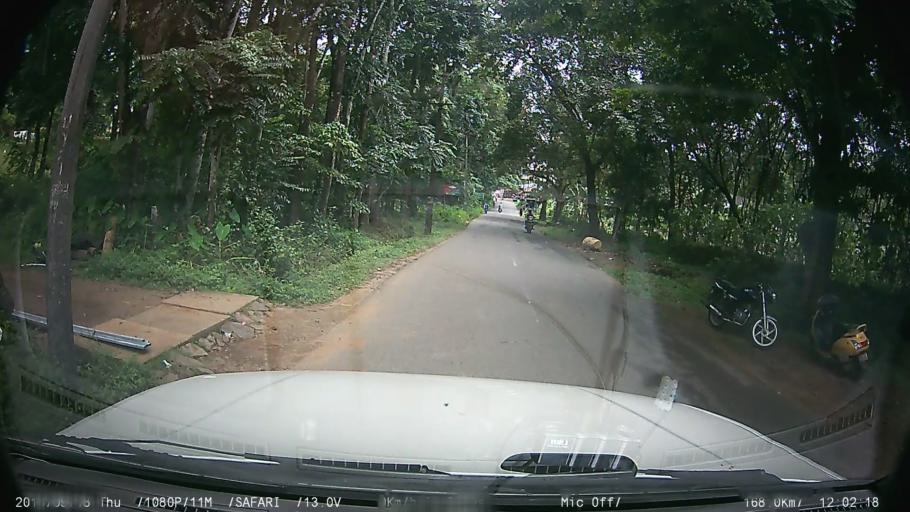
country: IN
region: Kerala
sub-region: Ernakulam
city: Kotamangalam
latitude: 10.1075
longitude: 76.6714
